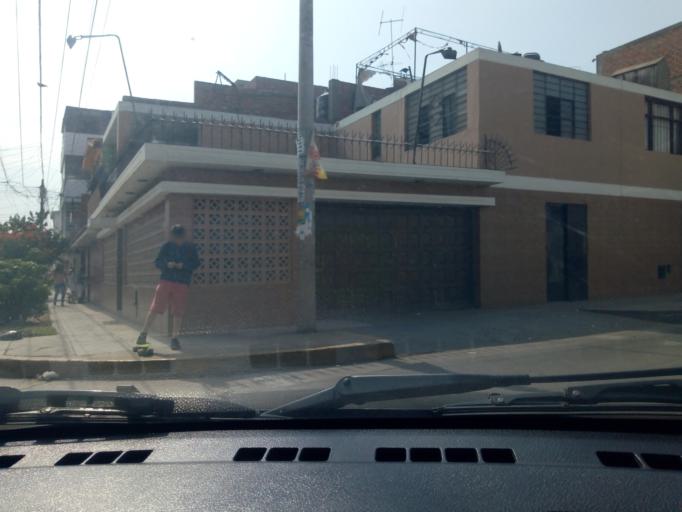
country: PE
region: Lima
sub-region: Lima
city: Independencia
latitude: -11.9951
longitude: -77.0732
